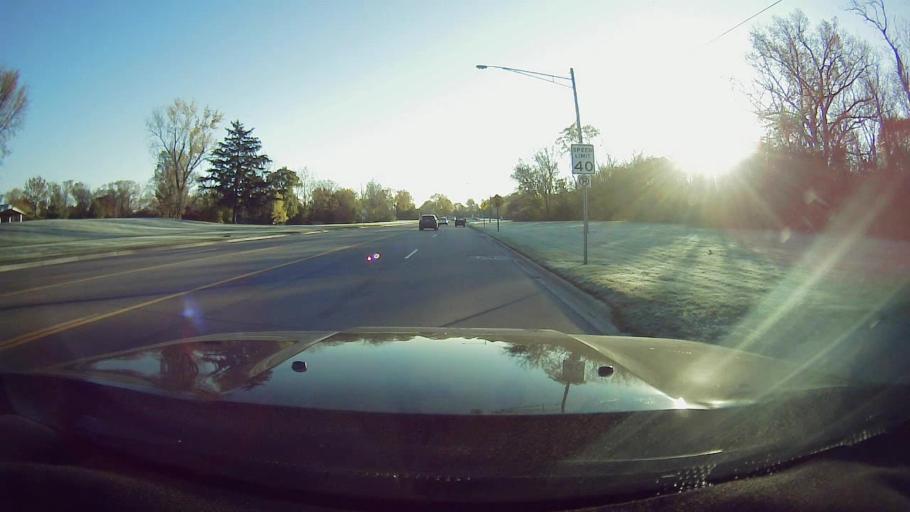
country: US
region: Michigan
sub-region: Macomb County
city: Sterling Heights
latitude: 42.5500
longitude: -83.0803
